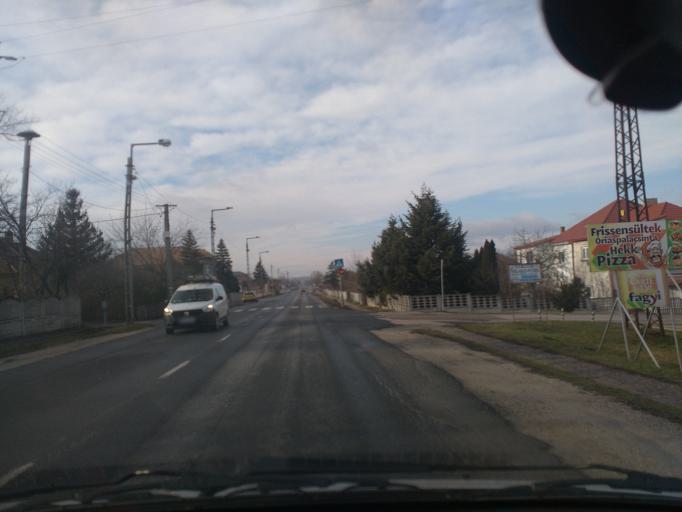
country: HU
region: Komarom-Esztergom
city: Tokod
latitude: 47.7317
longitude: 18.6926
